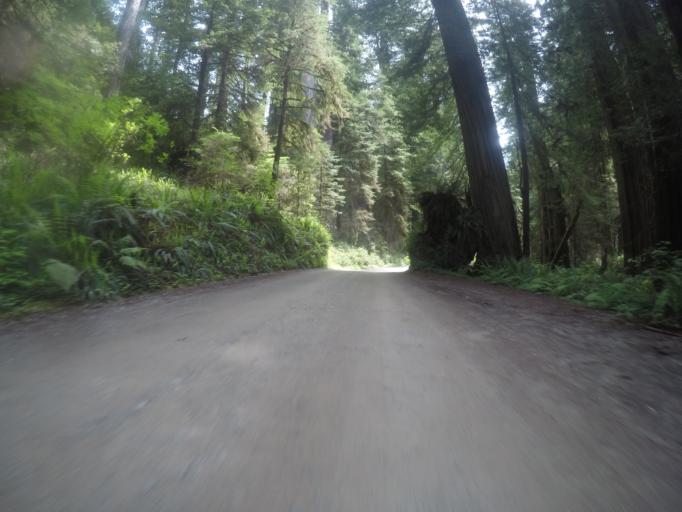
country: US
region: California
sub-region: Del Norte County
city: Bertsch-Oceanview
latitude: 41.7660
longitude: -124.1191
